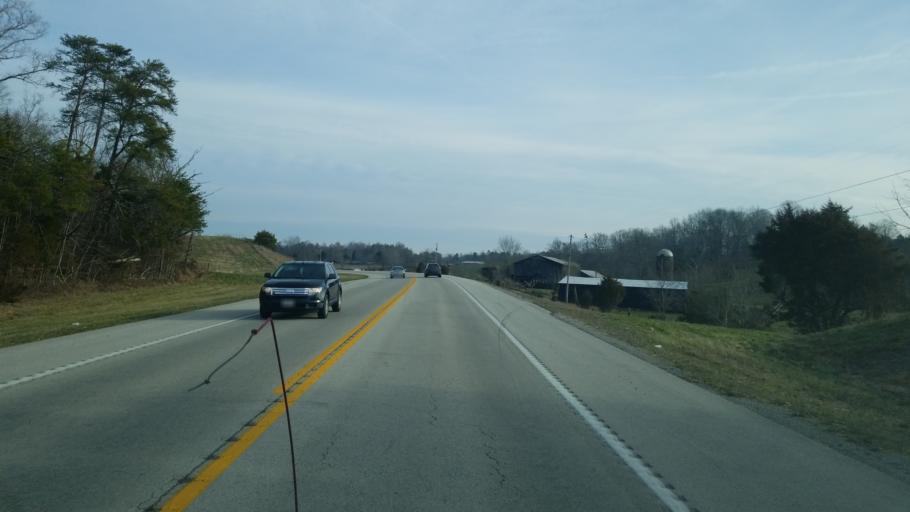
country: US
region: Kentucky
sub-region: Russell County
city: Russell Springs
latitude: 37.1655
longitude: -85.0089
